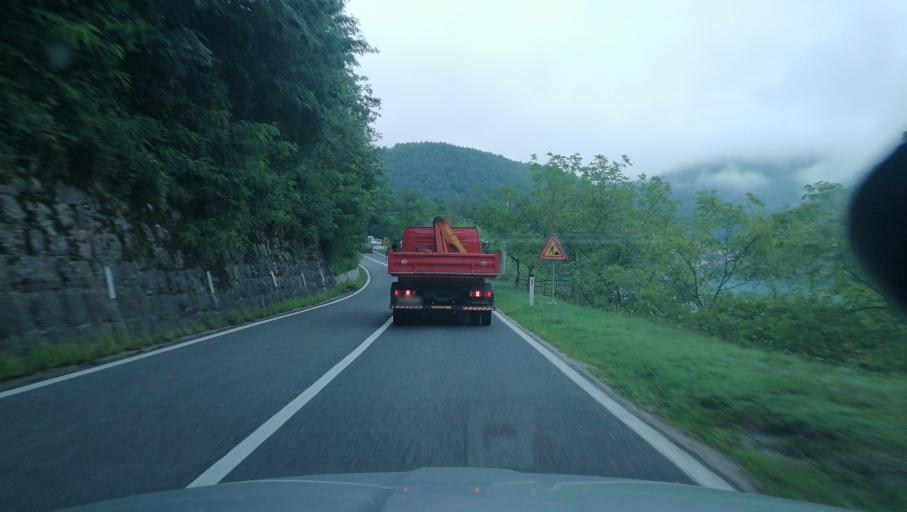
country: BA
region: Federation of Bosnia and Herzegovina
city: Jablanica
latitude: 43.7212
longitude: 17.7067
